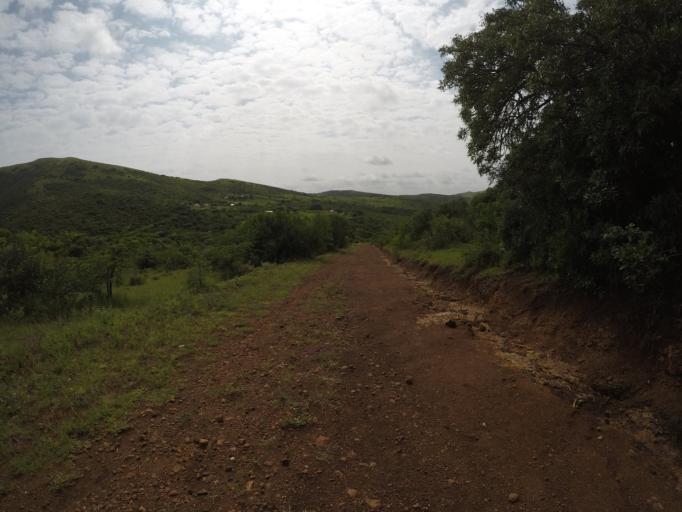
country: ZA
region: KwaZulu-Natal
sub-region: uThungulu District Municipality
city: Empangeni
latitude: -28.6148
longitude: 31.9027
